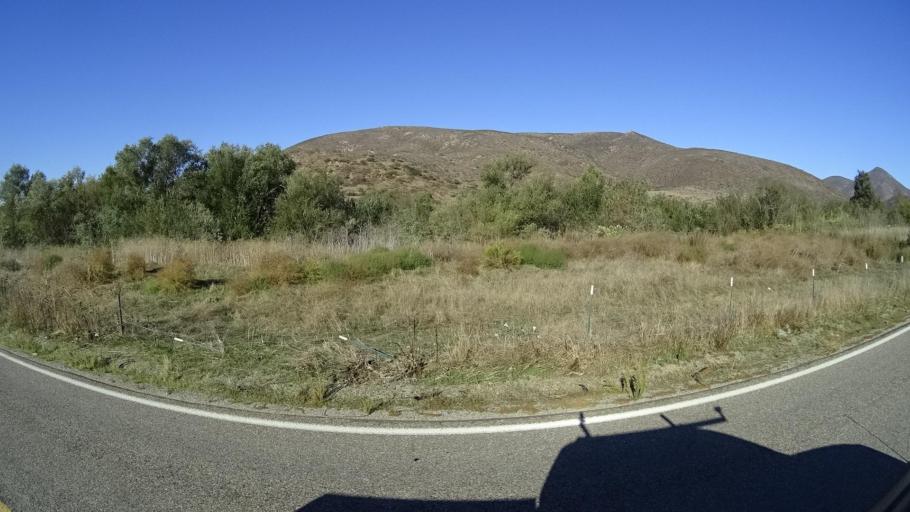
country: US
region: California
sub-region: San Diego County
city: Jamul
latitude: 32.6460
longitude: -116.8696
